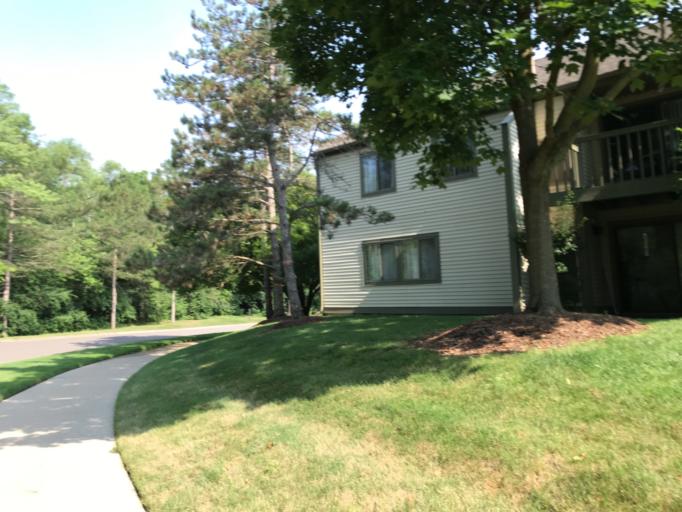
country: US
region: Michigan
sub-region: Washtenaw County
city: Ann Arbor
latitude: 42.2417
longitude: -83.7156
